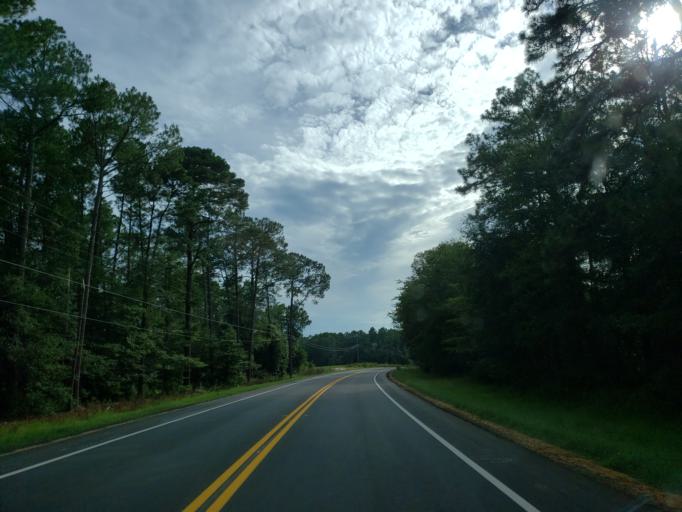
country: US
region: Georgia
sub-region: Irwin County
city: Ocilla
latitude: 31.5664
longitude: -83.3134
